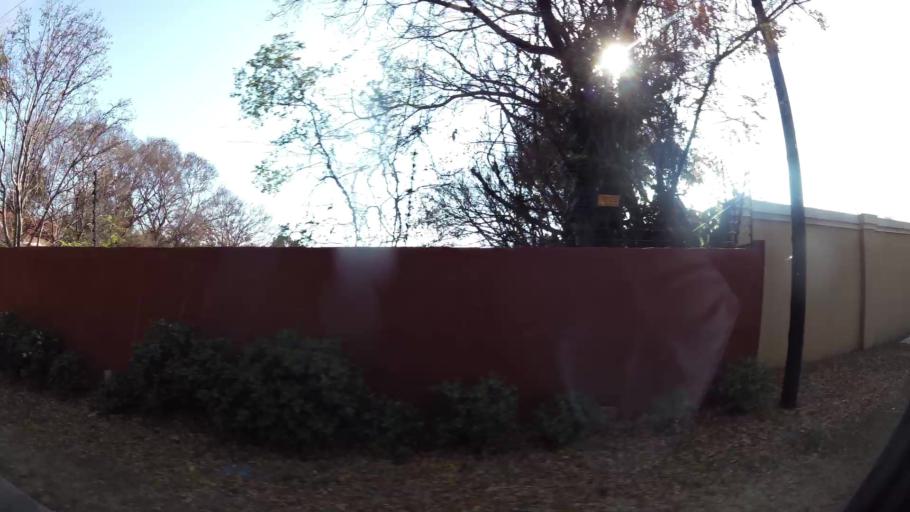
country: ZA
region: Gauteng
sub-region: City of Johannesburg Metropolitan Municipality
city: Roodepoort
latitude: -26.0967
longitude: 27.9698
